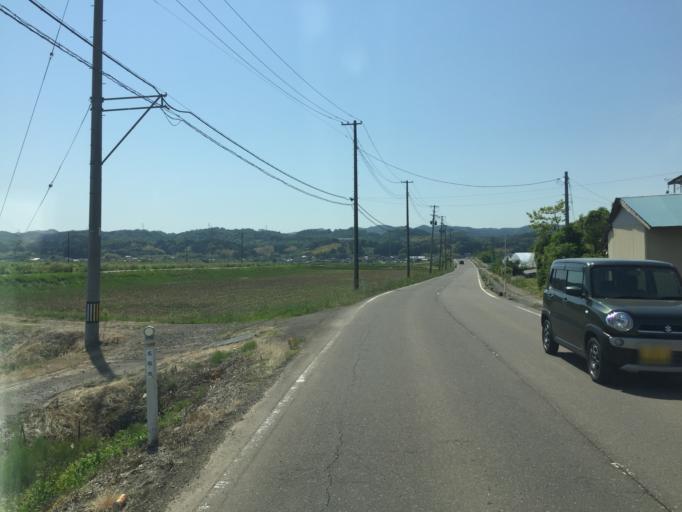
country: JP
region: Miyagi
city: Iwanuma
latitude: 38.1493
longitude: 140.8610
